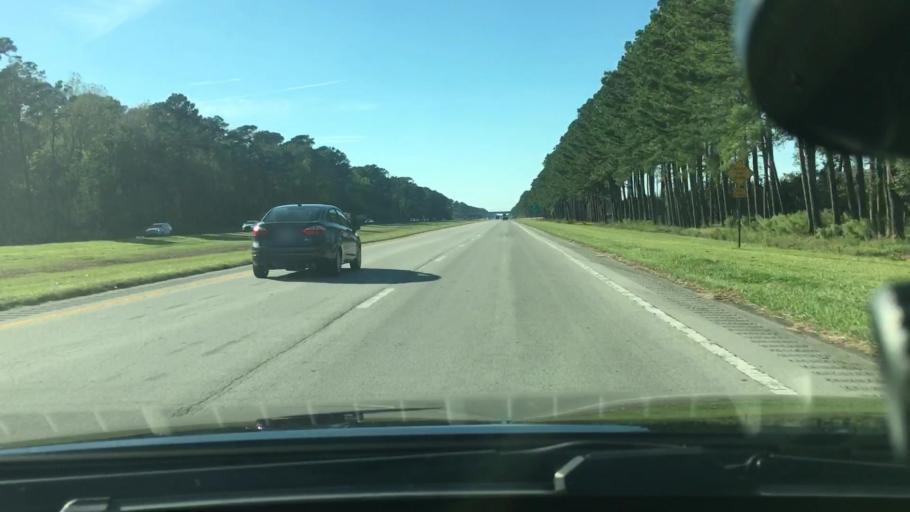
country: US
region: North Carolina
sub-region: Craven County
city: Trent Woods
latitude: 35.1235
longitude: -77.1219
